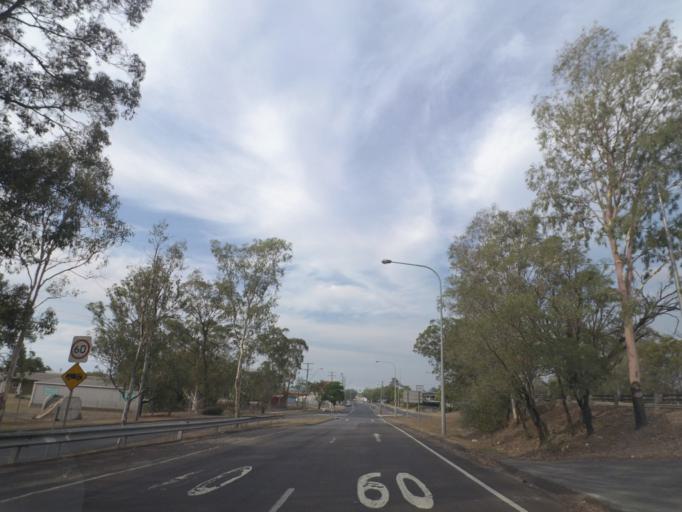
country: AU
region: Queensland
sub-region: Brisbane
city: Rocklea
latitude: -27.5447
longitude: 153.0105
